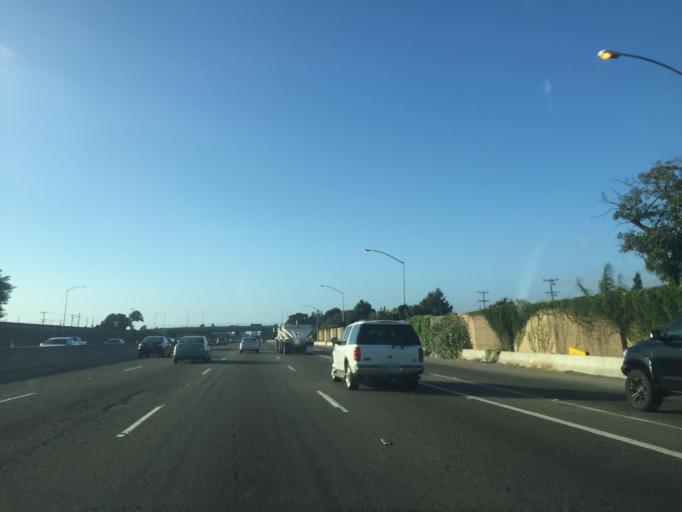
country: US
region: California
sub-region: Alameda County
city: San Leandro
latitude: 37.7167
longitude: -122.1740
